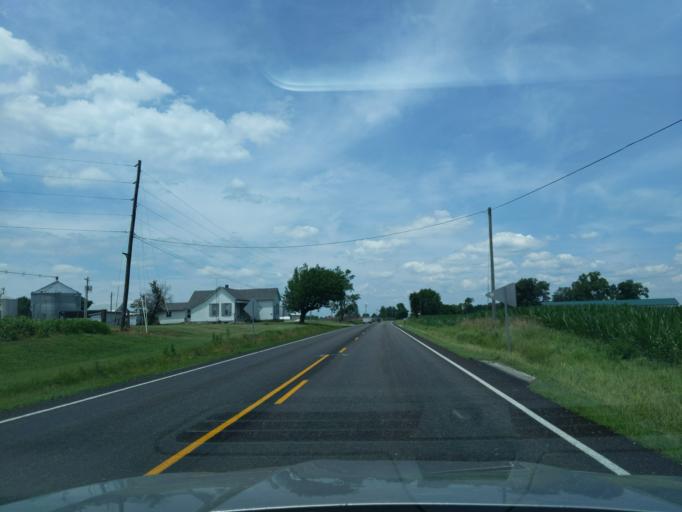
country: US
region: Indiana
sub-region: Ripley County
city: Osgood
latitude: 39.2096
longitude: -85.3313
